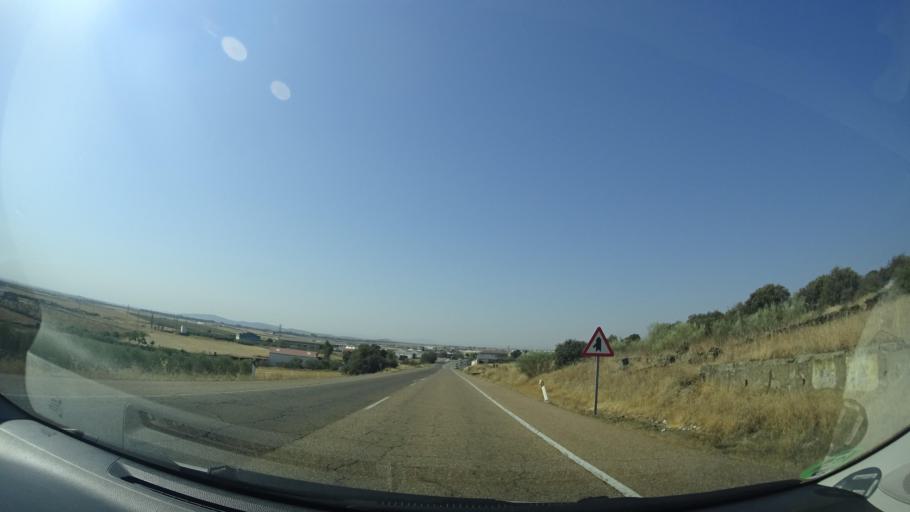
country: ES
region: Extremadura
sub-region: Provincia de Caceres
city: Escurial
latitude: 39.1639
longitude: -5.8987
